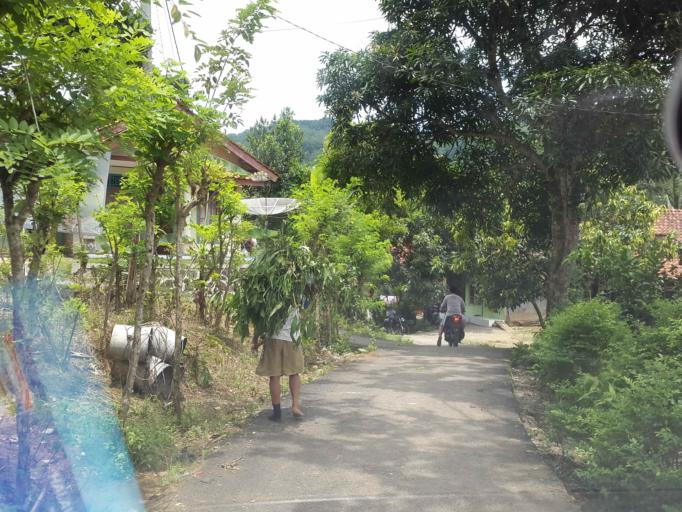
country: ID
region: Central Java
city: Muara
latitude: -7.2594
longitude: 108.8849
